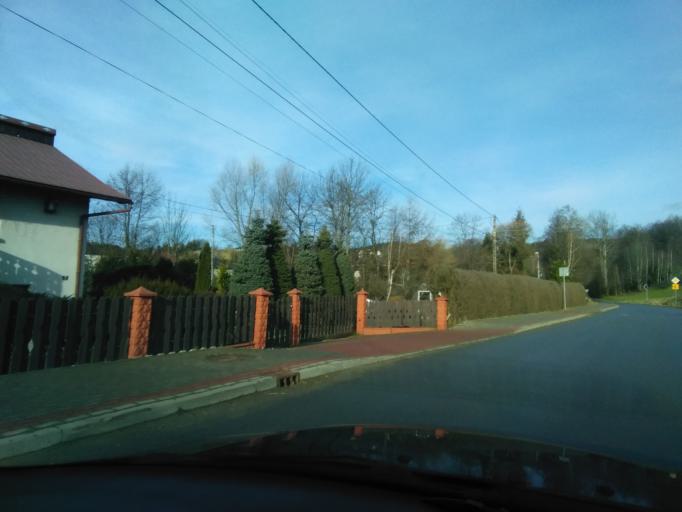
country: PL
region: Subcarpathian Voivodeship
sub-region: Powiat krosnienski
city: Korczyna
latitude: 49.7208
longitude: 21.8073
